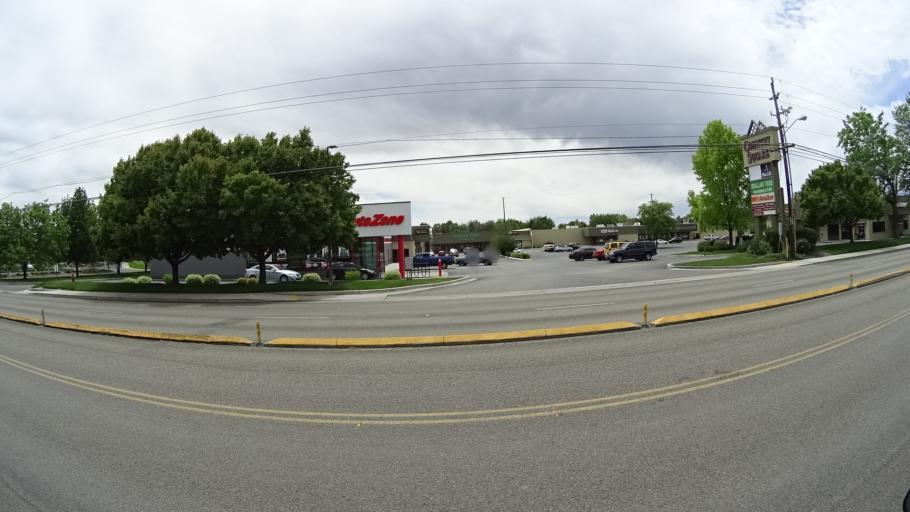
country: US
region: Idaho
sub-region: Ada County
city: Garden City
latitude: 43.5905
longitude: -116.3120
